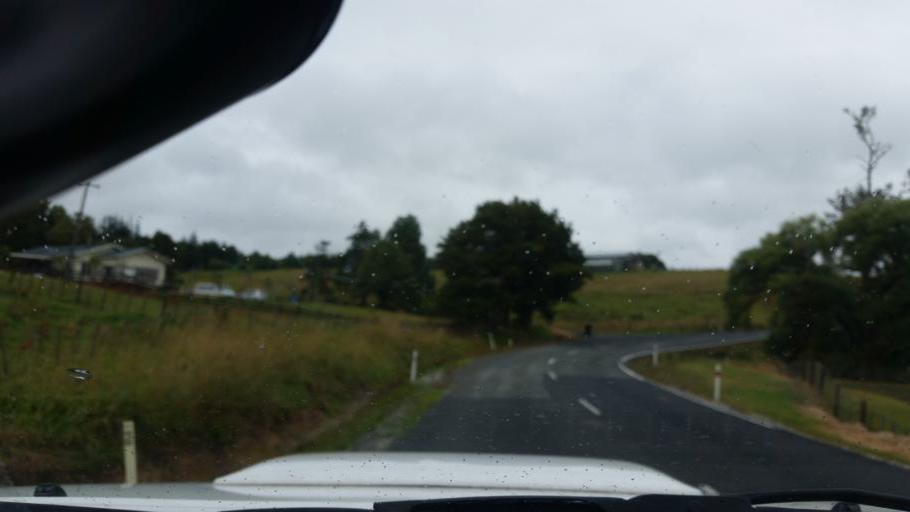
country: NZ
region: Auckland
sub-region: Auckland
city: Wellsford
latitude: -36.1706
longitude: 174.4656
